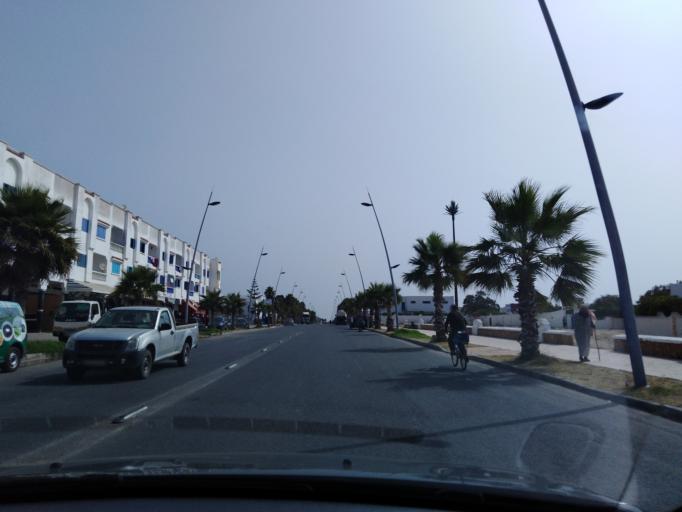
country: MA
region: Doukkala-Abda
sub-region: Safi
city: Safi
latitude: 32.7299
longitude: -9.0378
